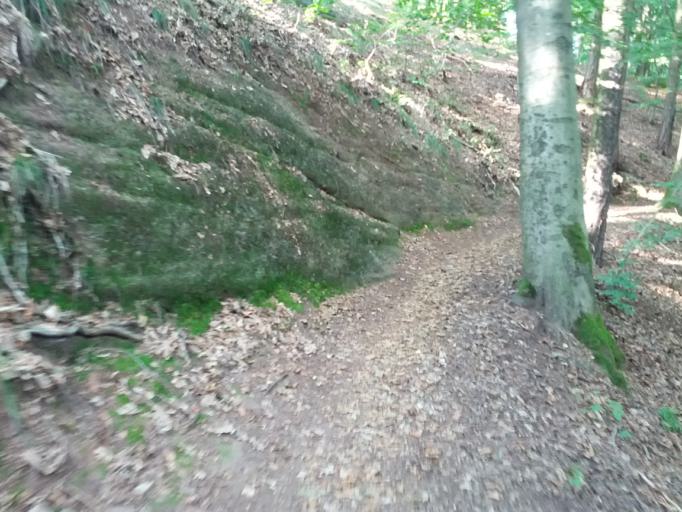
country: DE
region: Thuringia
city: Eisenach
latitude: 50.9517
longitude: 10.3293
